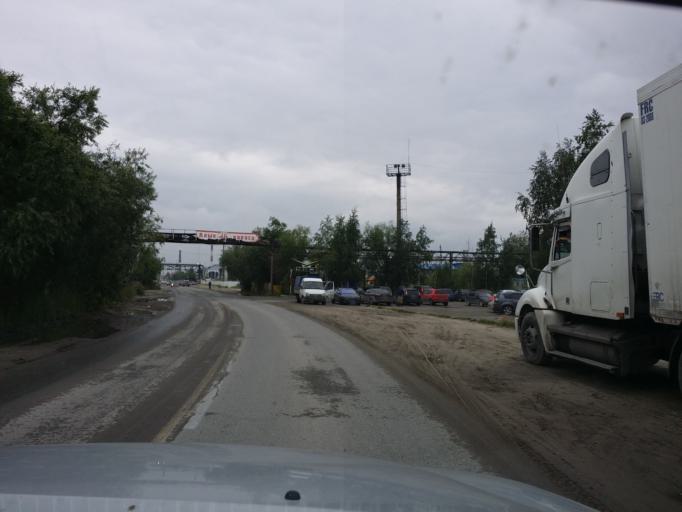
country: RU
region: Khanty-Mansiyskiy Avtonomnyy Okrug
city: Nizhnevartovsk
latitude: 60.9512
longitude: 76.5478
